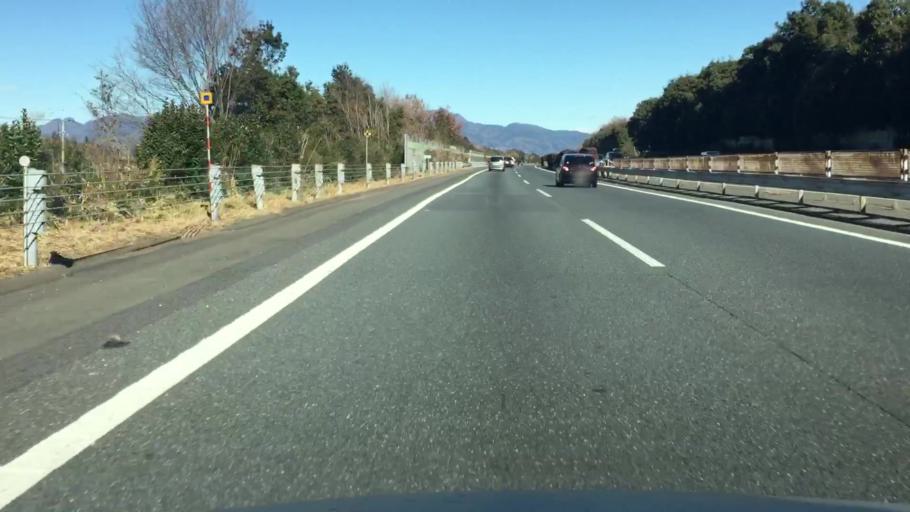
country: JP
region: Gunma
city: Kanekomachi
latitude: 36.4363
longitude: 139.0143
